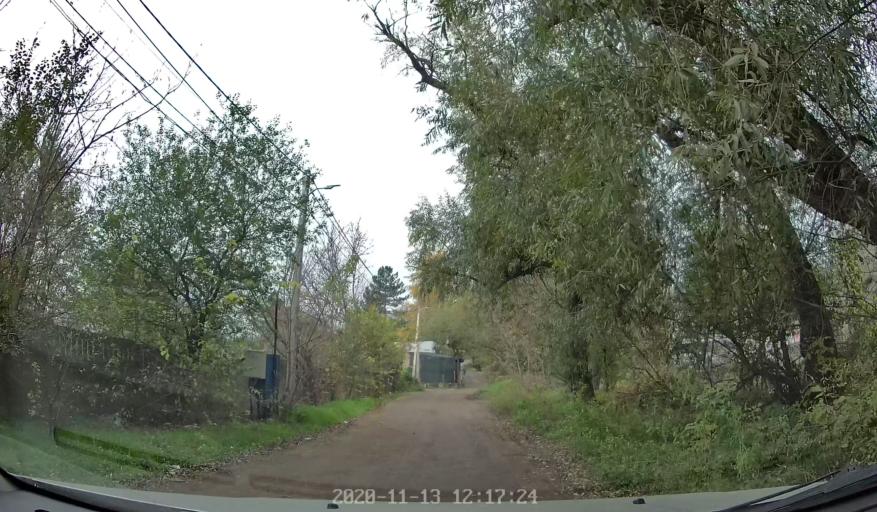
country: MD
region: Laloveni
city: Ialoveni
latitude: 46.9481
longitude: 28.8369
